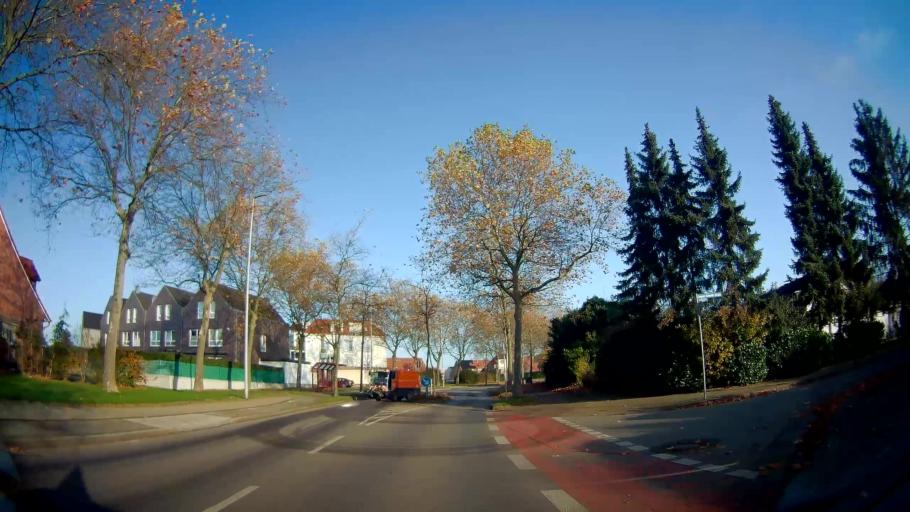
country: DE
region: North Rhine-Westphalia
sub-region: Regierungsbezirk Munster
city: Gladbeck
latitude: 51.5875
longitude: 6.9576
